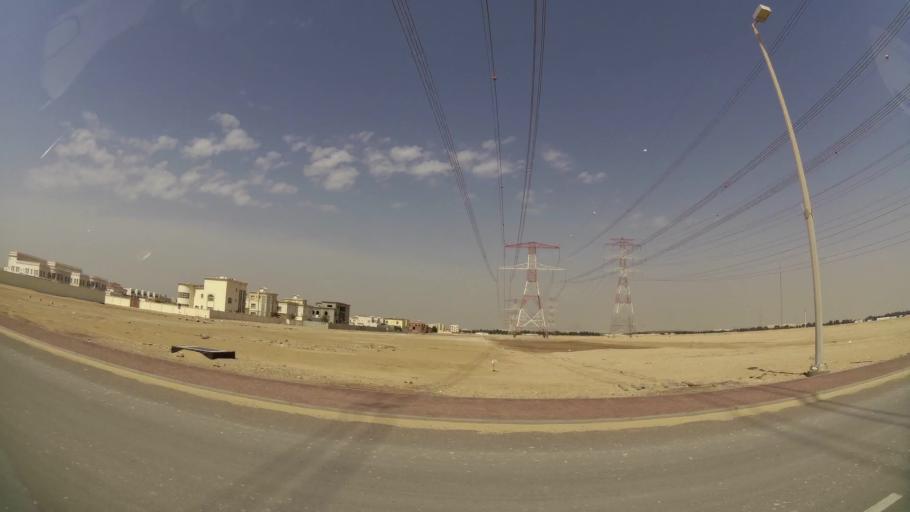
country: AE
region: Abu Dhabi
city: Abu Dhabi
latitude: 24.3168
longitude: 54.5793
